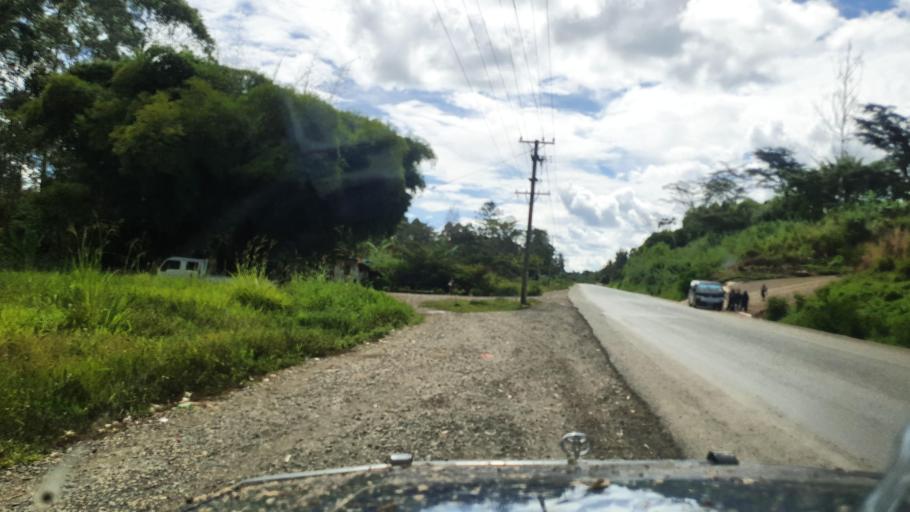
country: PG
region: Jiwaka
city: Minj
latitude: -5.9382
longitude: 144.8076
